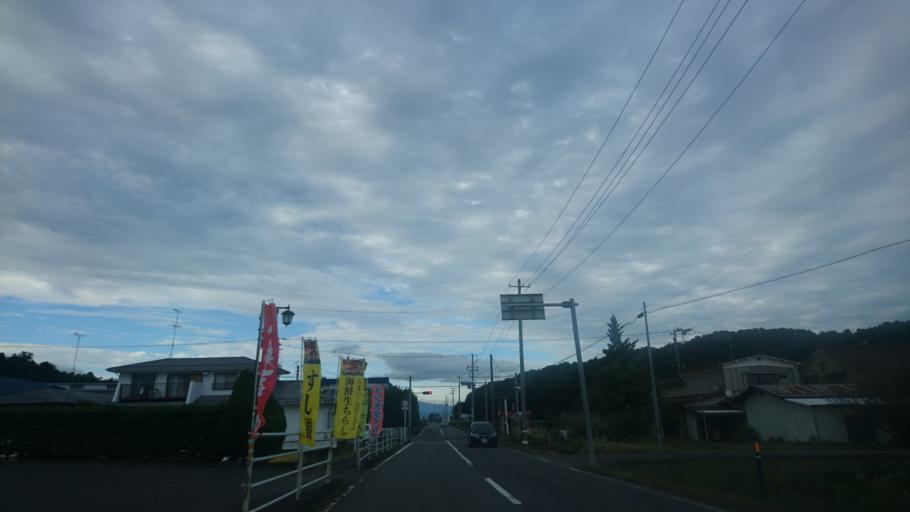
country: JP
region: Fukushima
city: Sukagawa
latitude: 37.3273
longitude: 140.2670
